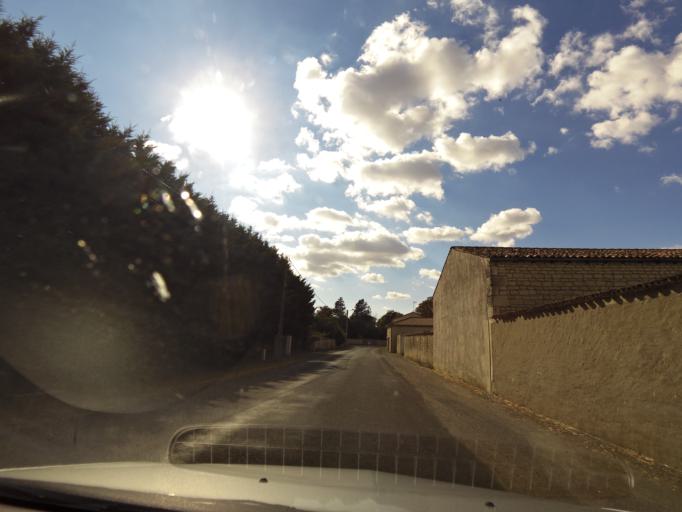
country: FR
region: Poitou-Charentes
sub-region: Departement des Deux-Sevres
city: Beauvoir-sur-Niort
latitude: 46.1544
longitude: -0.4827
